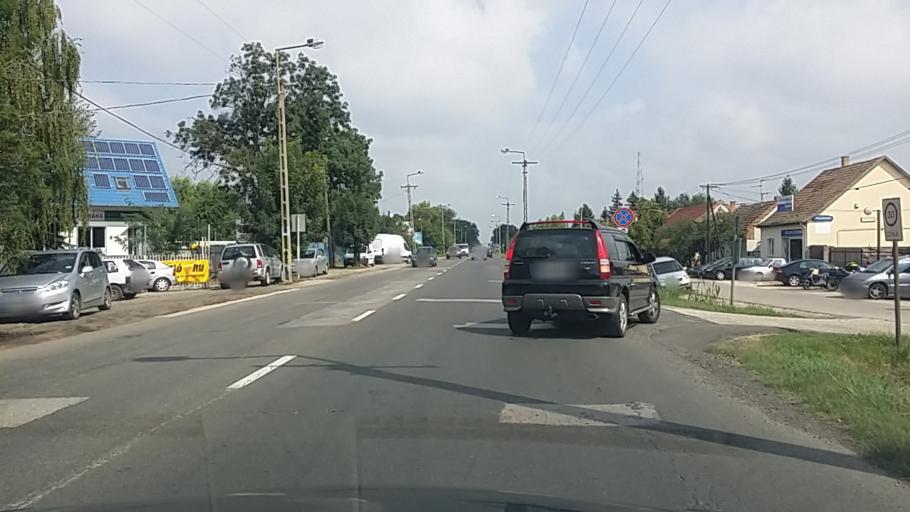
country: HU
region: Csongrad
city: Szeged
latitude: 46.2838
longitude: 20.1704
